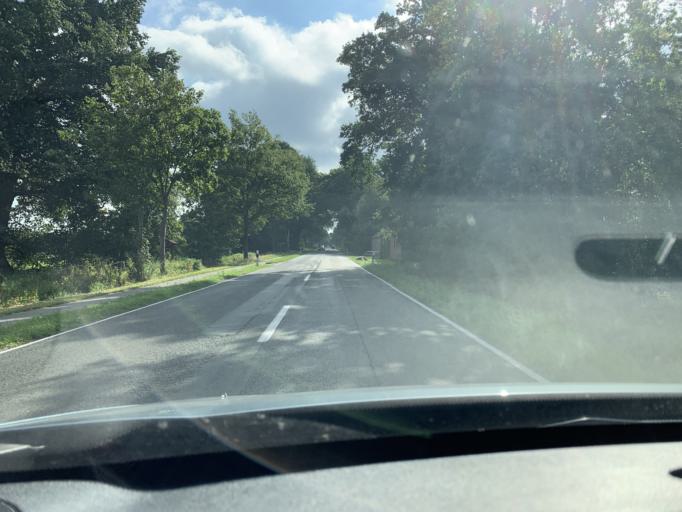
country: DE
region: Lower Saxony
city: Wardenburg
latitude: 53.0718
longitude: 8.1533
